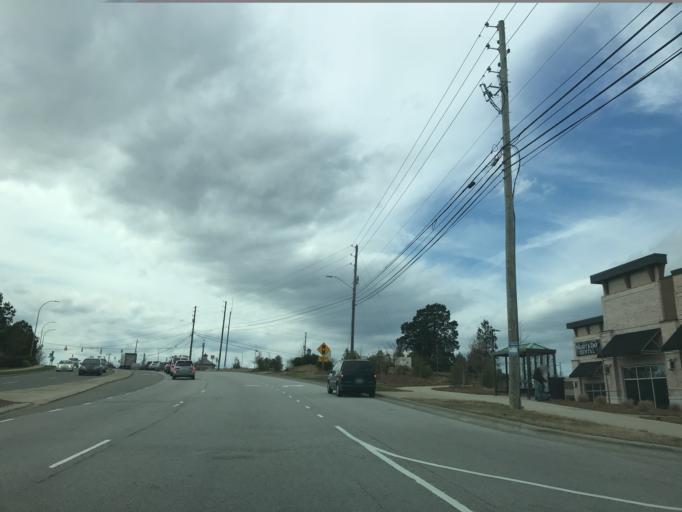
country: US
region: North Carolina
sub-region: Wake County
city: Morrisville
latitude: 35.7922
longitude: -78.8449
